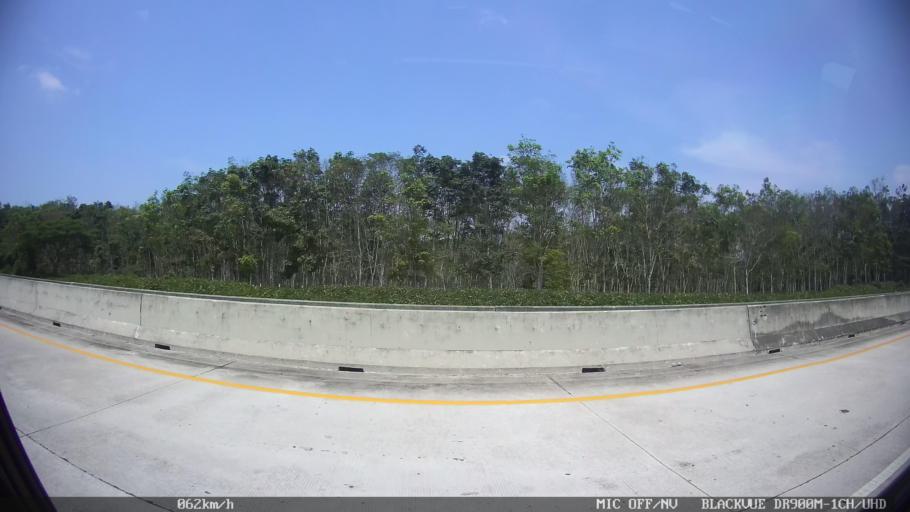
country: ID
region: Lampung
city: Kedaton
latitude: -5.3576
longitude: 105.3245
